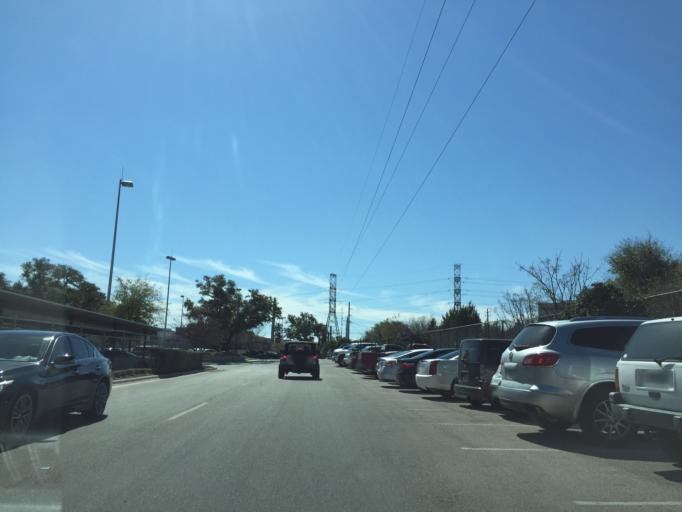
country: US
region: Texas
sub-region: Williamson County
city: Jollyville
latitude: 30.4009
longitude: -97.7281
